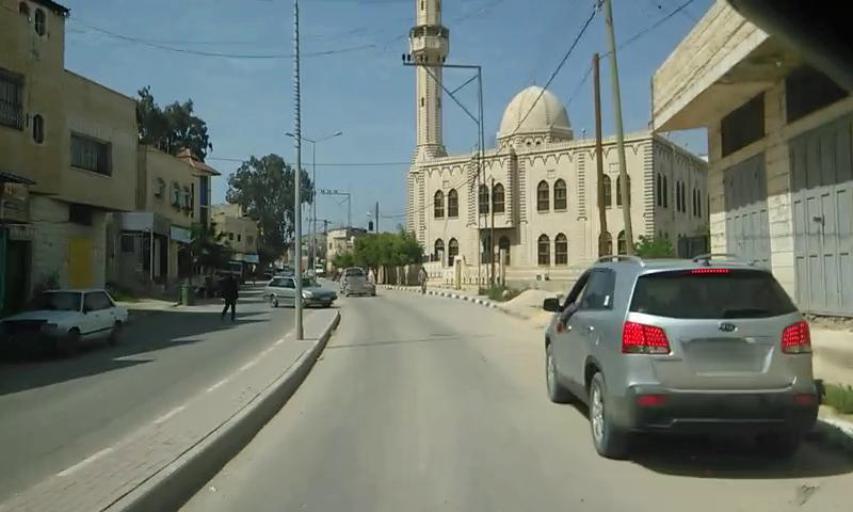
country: PS
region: West Bank
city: Qabatiyah
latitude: 32.4096
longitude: 35.2856
